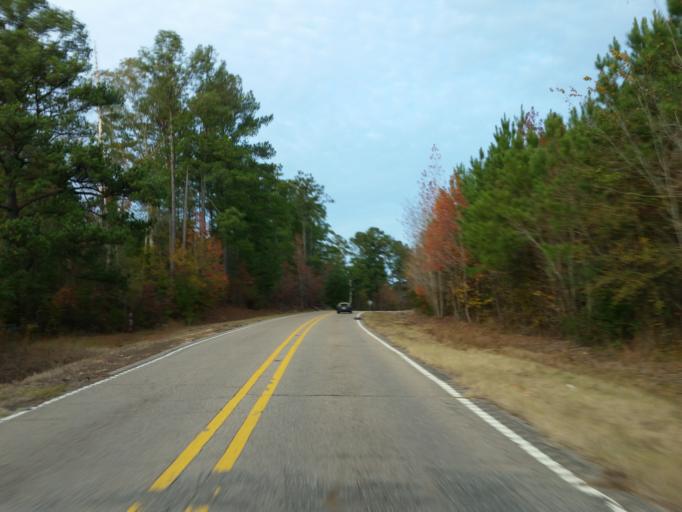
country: US
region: Mississippi
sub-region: Lauderdale County
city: Marion
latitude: 32.4167
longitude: -88.5394
